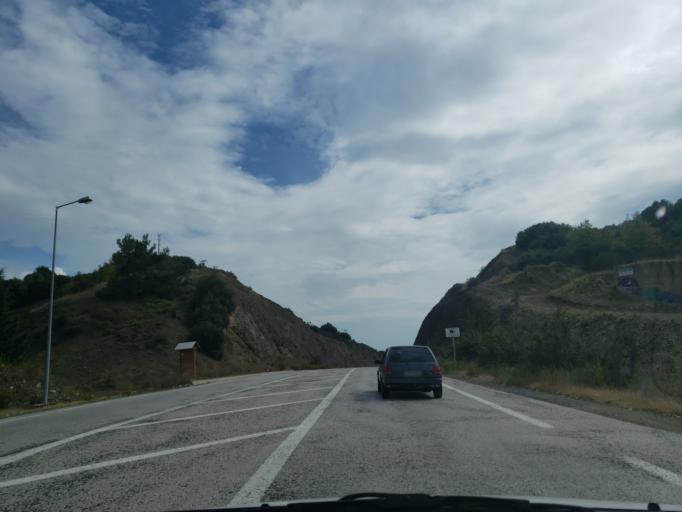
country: GR
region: Central Greece
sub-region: Nomos Fthiotidos
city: Stavros
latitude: 38.9884
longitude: 22.3751
